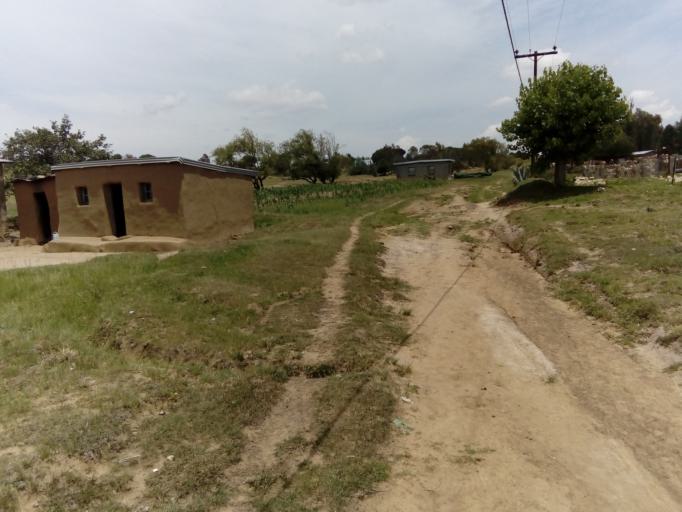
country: LS
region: Mafeteng
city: Mafeteng
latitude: -29.6965
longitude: 27.4370
